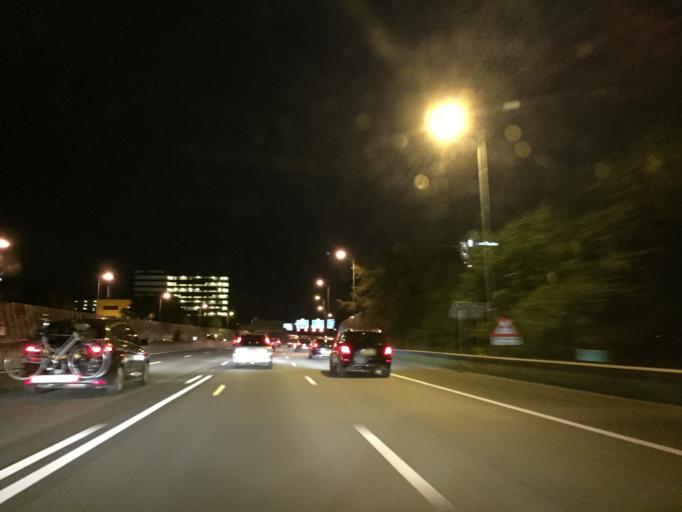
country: NL
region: North Holland
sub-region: Gemeente Amsterdam
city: Amsterdam
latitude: 52.3533
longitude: 4.8424
